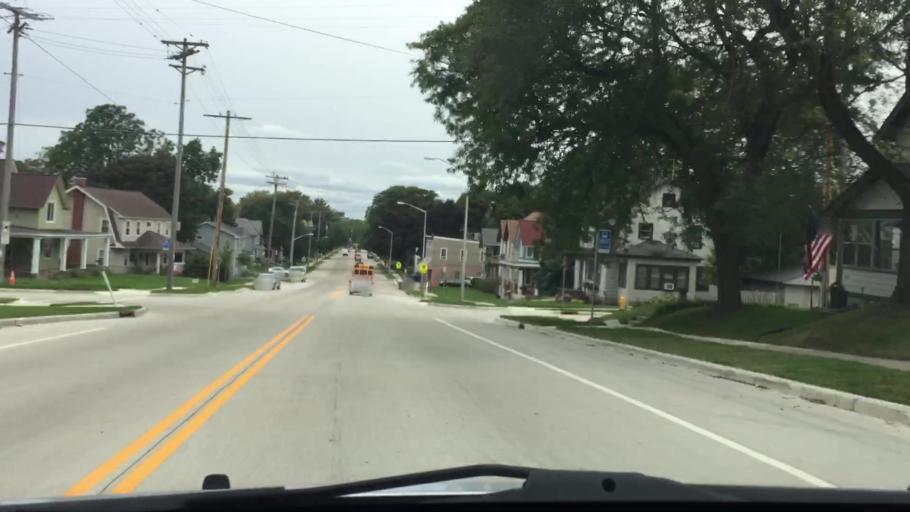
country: US
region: Wisconsin
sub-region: Waukesha County
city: Waukesha
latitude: 43.0132
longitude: -88.2148
